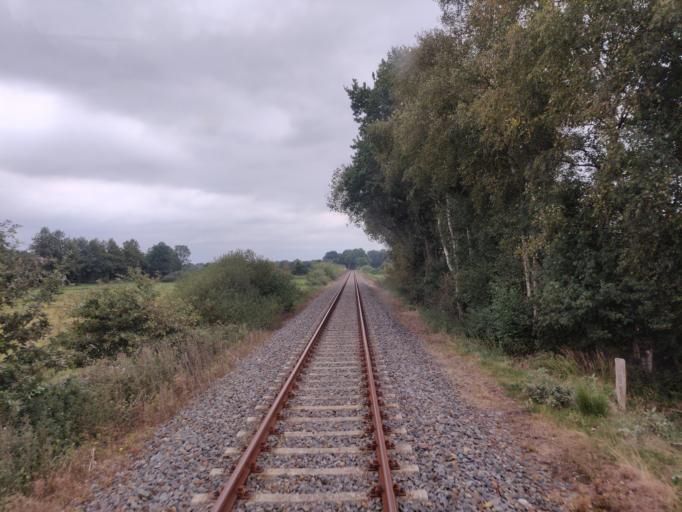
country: DE
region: Lower Saxony
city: Gnarrenburg
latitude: 53.3425
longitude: 8.9982
